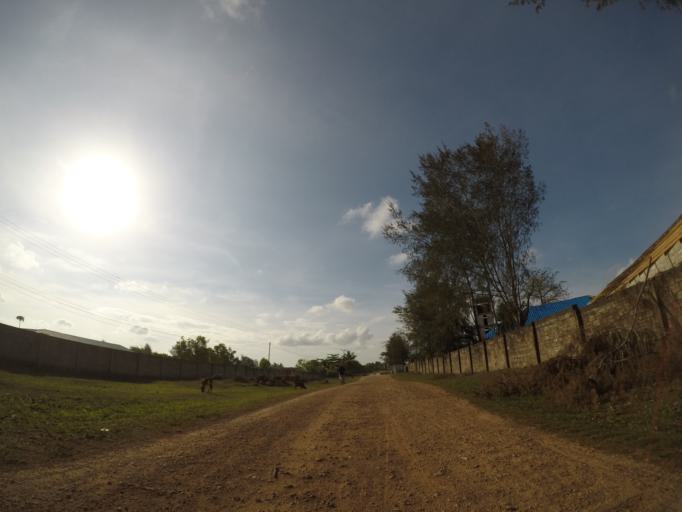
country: TZ
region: Zanzibar Central/South
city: Koani
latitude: -6.2095
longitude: 39.3183
